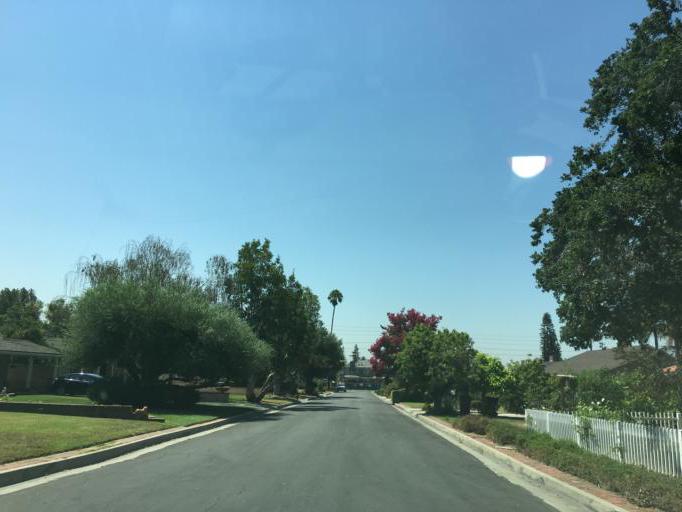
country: US
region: California
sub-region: Los Angeles County
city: San Marino
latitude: 34.1150
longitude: -118.0886
